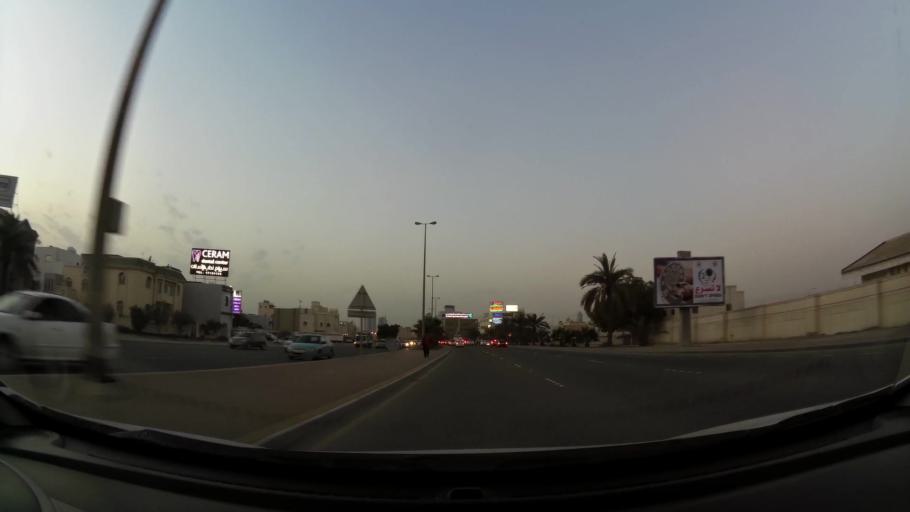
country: BH
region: Manama
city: Manama
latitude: 26.2062
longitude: 50.5674
